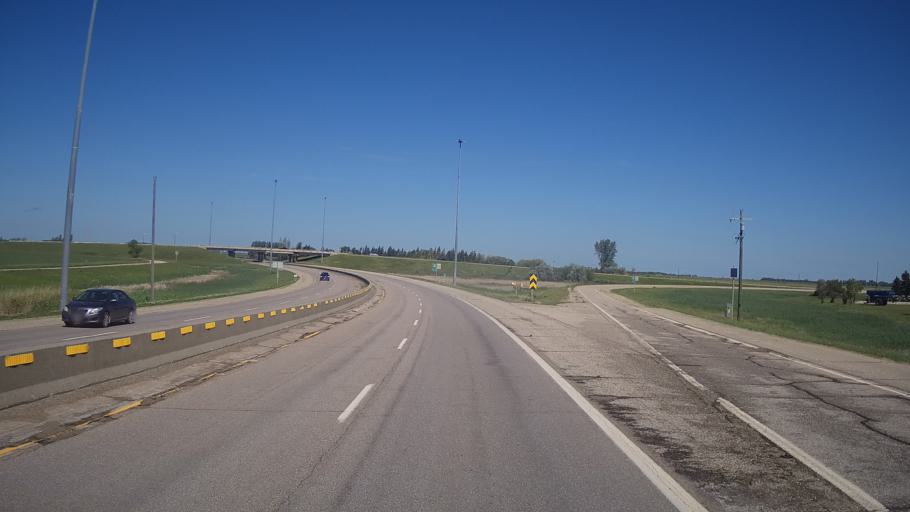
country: CA
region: Manitoba
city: Portage la Prairie
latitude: 49.9708
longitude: -98.3591
